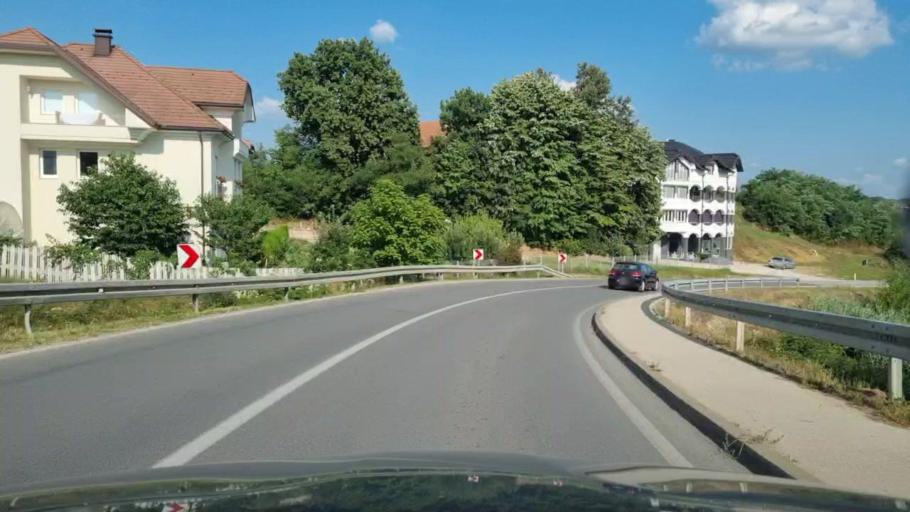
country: BA
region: Federation of Bosnia and Herzegovina
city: Gradacac
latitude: 44.8898
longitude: 18.4105
